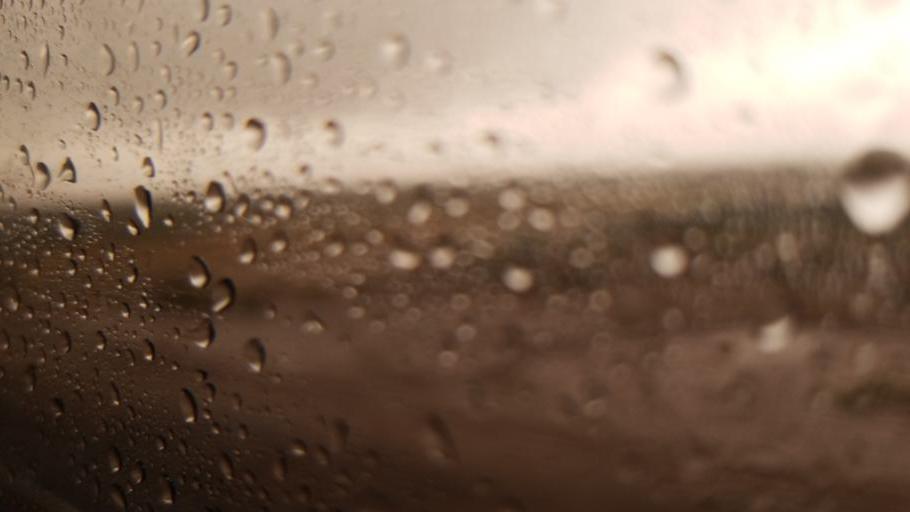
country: US
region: Arizona
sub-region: Navajo County
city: Joseph City
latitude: 34.9364
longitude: -110.3038
